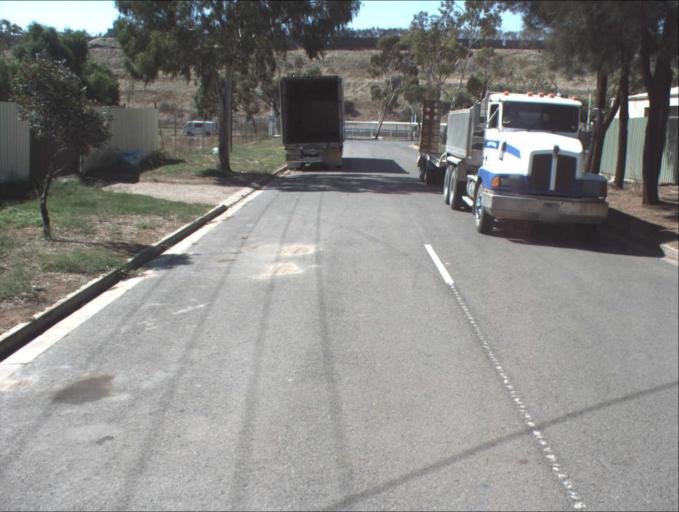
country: AU
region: South Australia
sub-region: Charles Sturt
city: Woodville North
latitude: -34.8380
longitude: 138.5532
